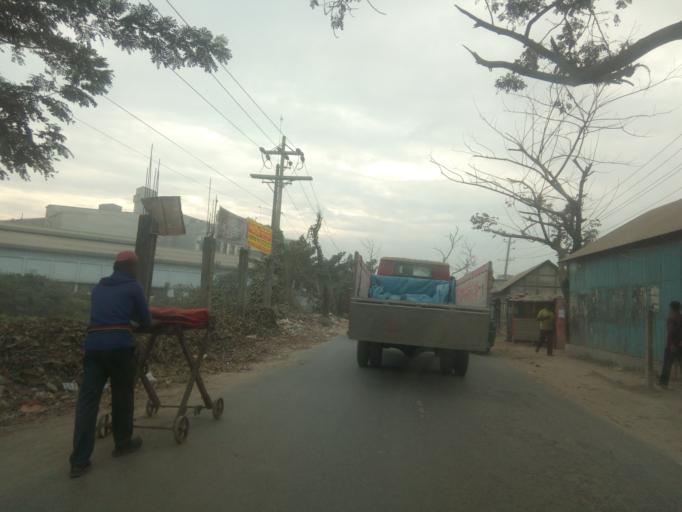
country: BD
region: Dhaka
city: Narayanganj
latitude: 23.5794
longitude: 90.5113
